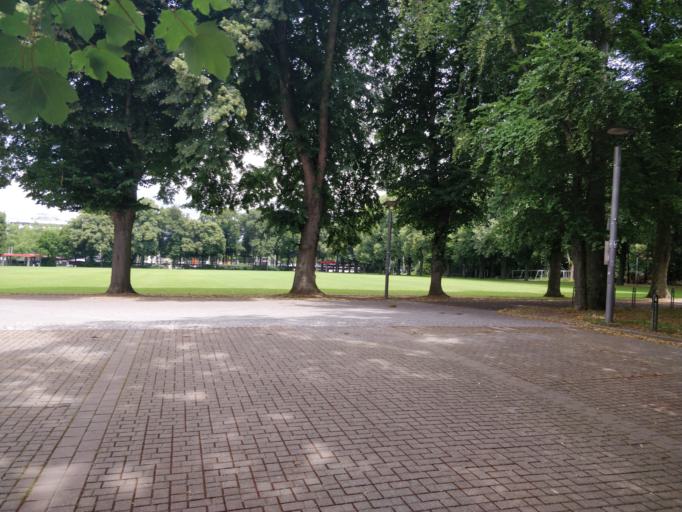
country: DE
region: North Rhine-Westphalia
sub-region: Regierungsbezirk Koln
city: Mengenich
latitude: 50.9348
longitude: 6.8768
